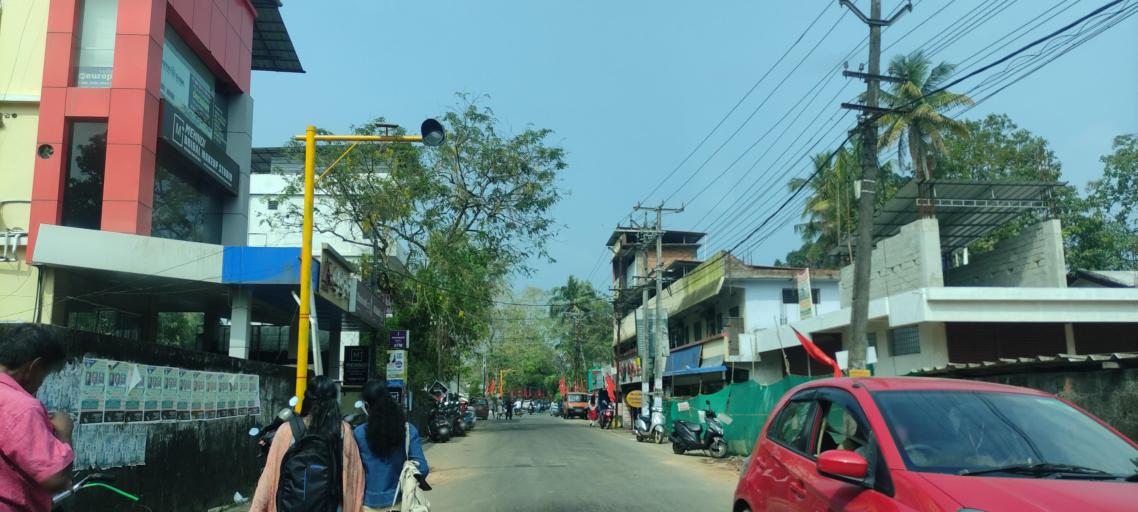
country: IN
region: Kerala
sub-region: Alappuzha
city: Shertallai
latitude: 9.6852
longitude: 76.3446
